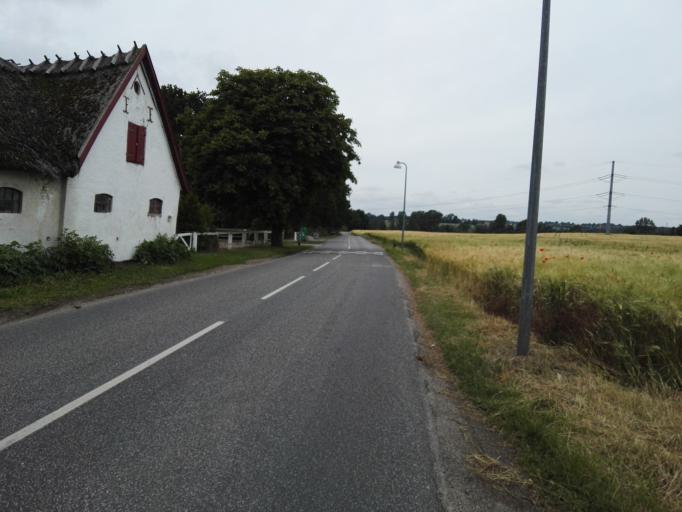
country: DK
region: Capital Region
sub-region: Egedal Kommune
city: Vekso
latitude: 55.7304
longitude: 12.2366
